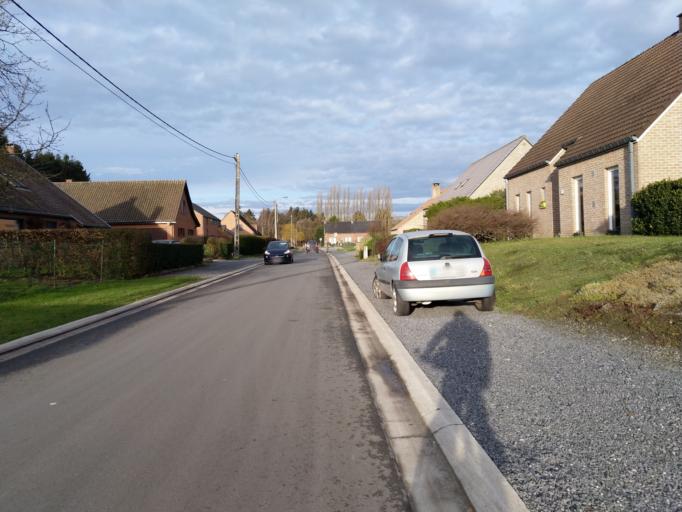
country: BE
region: Wallonia
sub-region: Province du Hainaut
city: Mons
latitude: 50.5189
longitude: 3.9982
